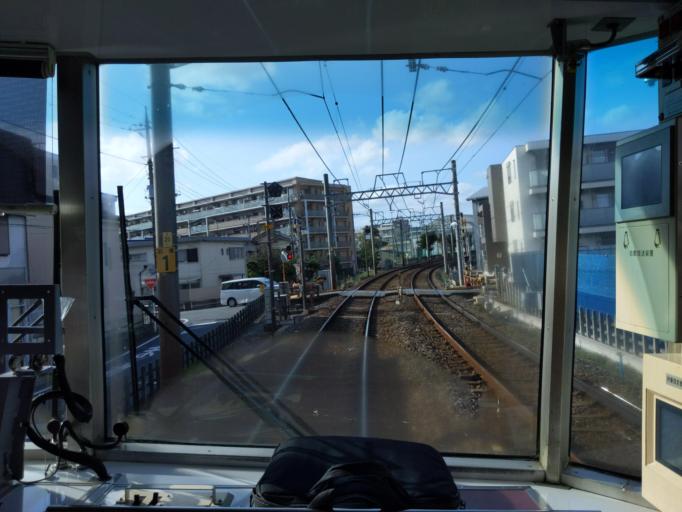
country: JP
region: Chiba
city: Kashiwa
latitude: 35.7933
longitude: 139.9687
